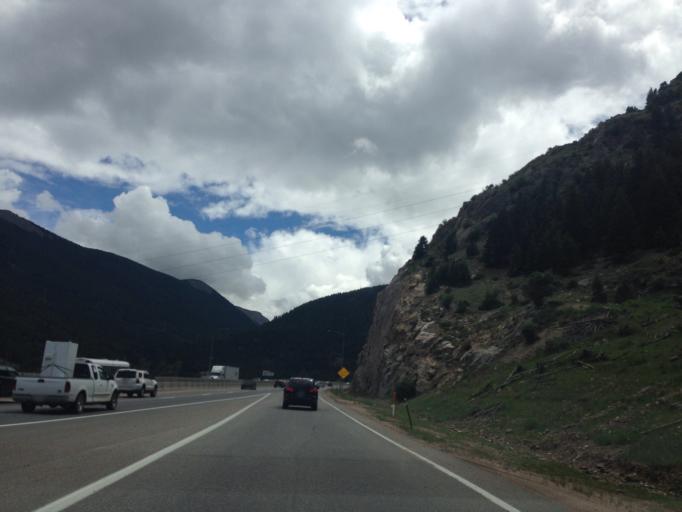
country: US
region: Colorado
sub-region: Clear Creek County
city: Georgetown
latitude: 39.7136
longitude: -105.6972
